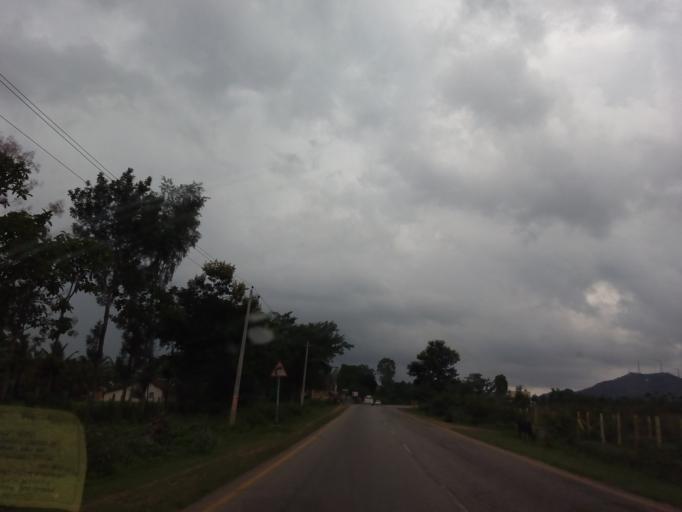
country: IN
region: Karnataka
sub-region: Hassan
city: Hassan
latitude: 13.0766
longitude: 76.0463
